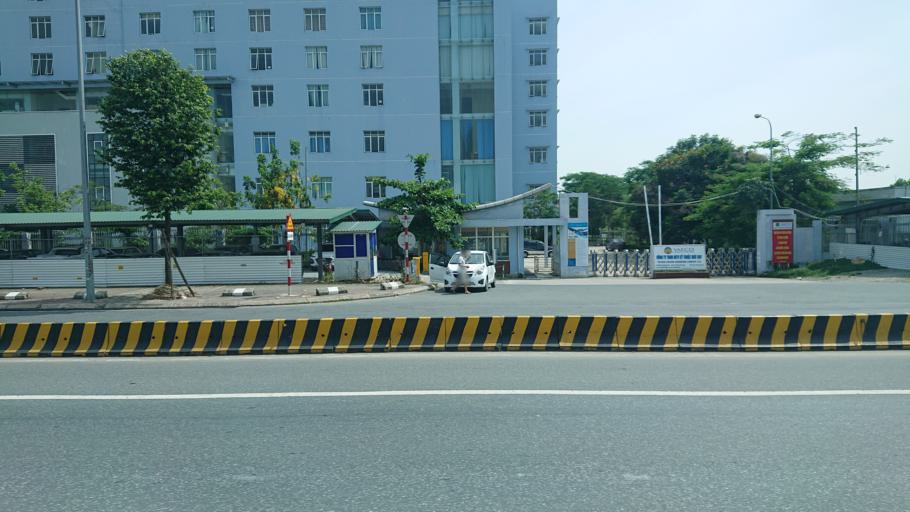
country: VN
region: Ha Noi
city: Soc Son
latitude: 21.2104
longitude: 105.8119
